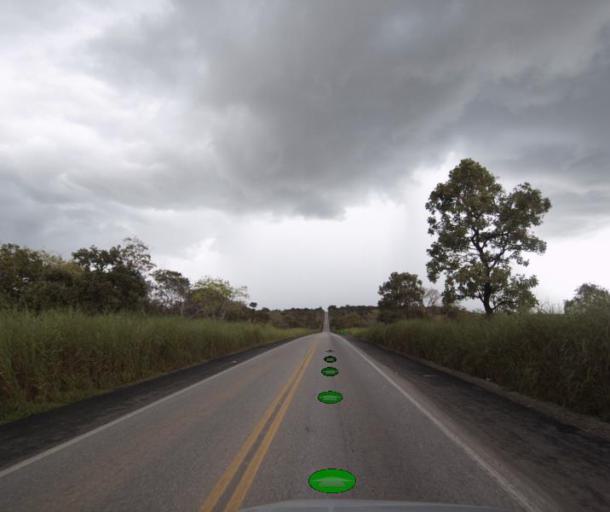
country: BR
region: Goias
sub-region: Uruacu
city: Uruacu
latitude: -14.2205
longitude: -49.1322
